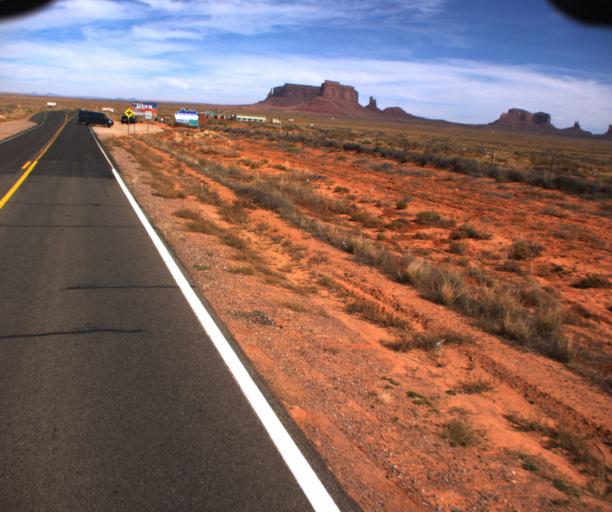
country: US
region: Arizona
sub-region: Navajo County
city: Kayenta
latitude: 36.9973
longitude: -110.1761
